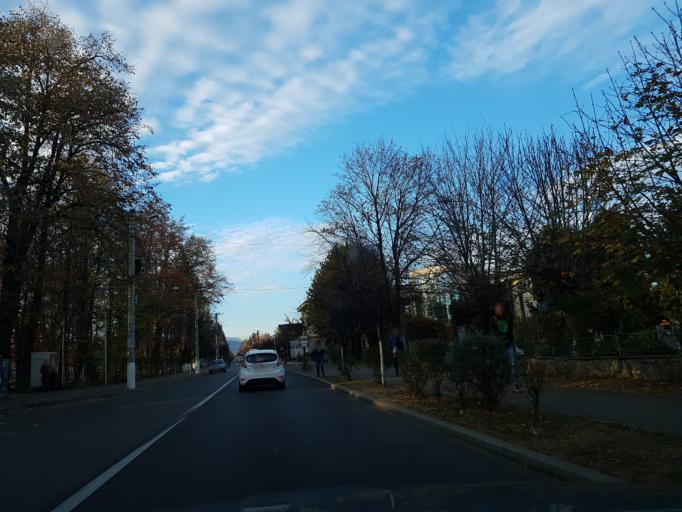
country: RO
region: Prahova
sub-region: Oras Breaza
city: Breaza
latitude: 45.1802
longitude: 25.6688
